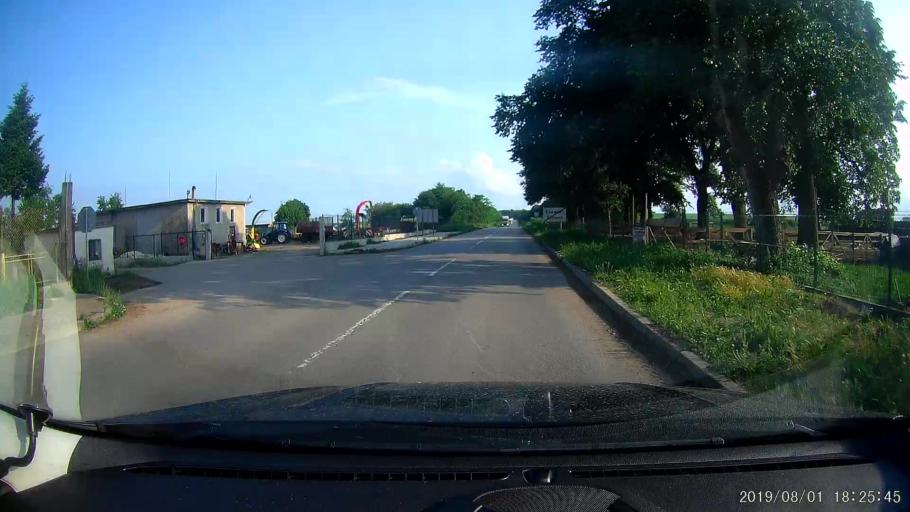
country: BG
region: Shumen
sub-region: Obshtina Venets
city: Venets
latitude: 43.6131
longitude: 26.9955
